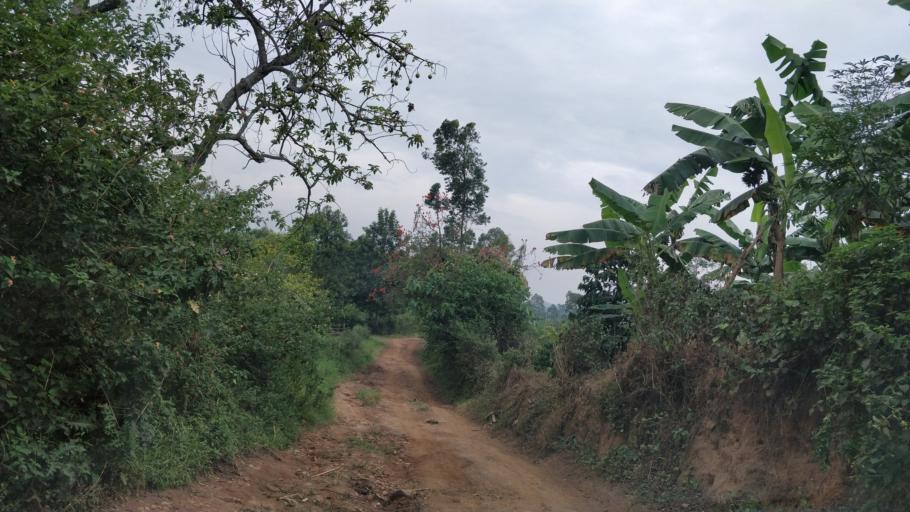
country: UG
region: Western Region
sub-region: Sheema District
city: Kibingo
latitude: -0.6950
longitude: 30.3906
